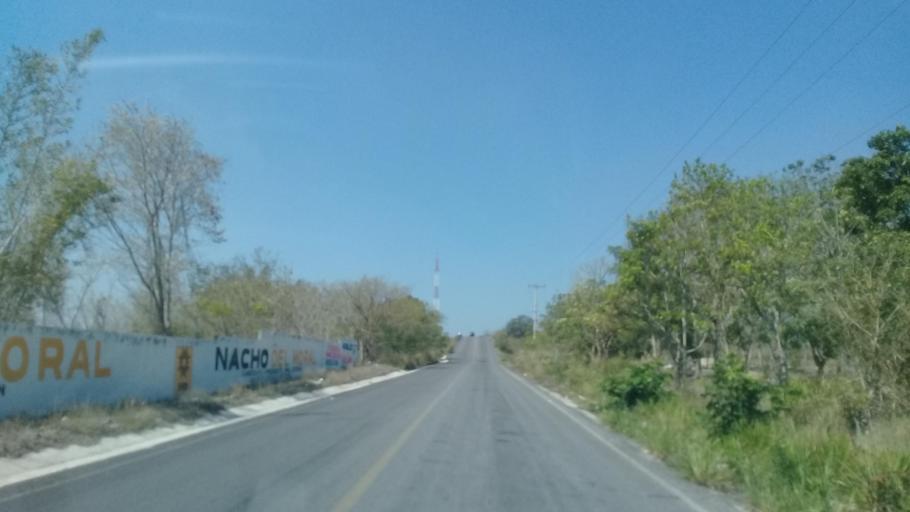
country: MX
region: Veracruz
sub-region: Emiliano Zapata
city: Plan del Rio
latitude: 19.3982
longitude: -96.6168
